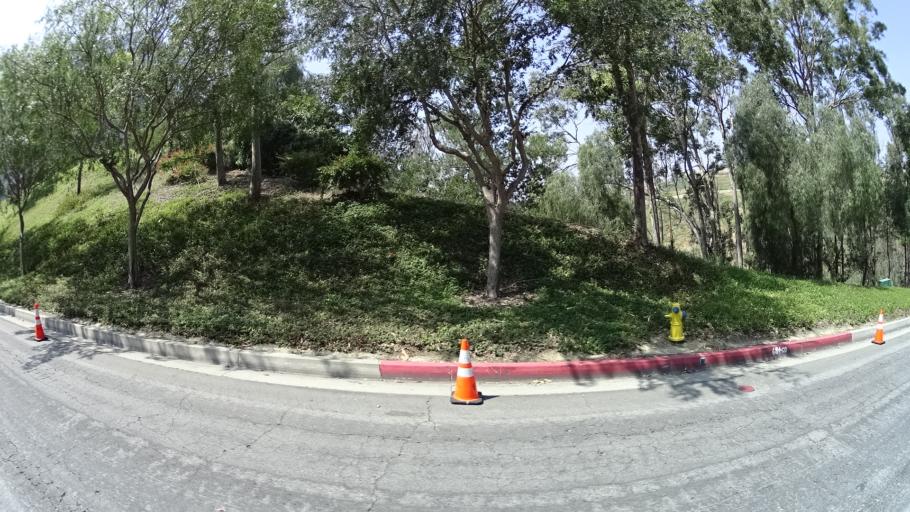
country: US
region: California
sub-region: Los Angeles County
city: Belvedere
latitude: 34.0532
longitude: -118.1628
